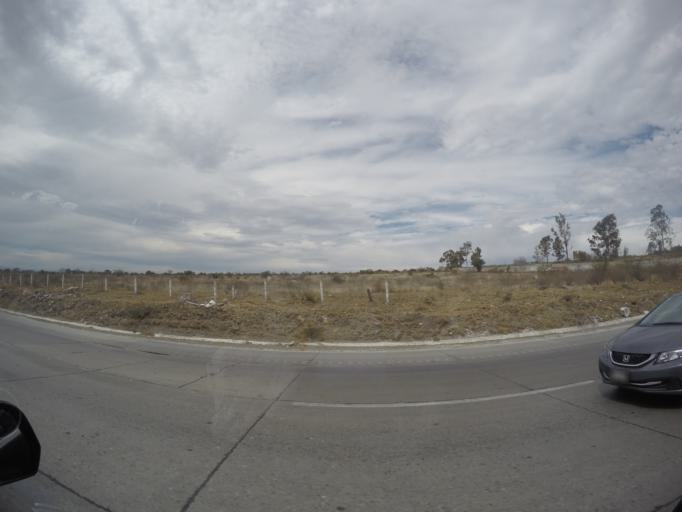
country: MX
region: Queretaro
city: San Juan del Rio
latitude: 20.3628
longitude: -99.9719
